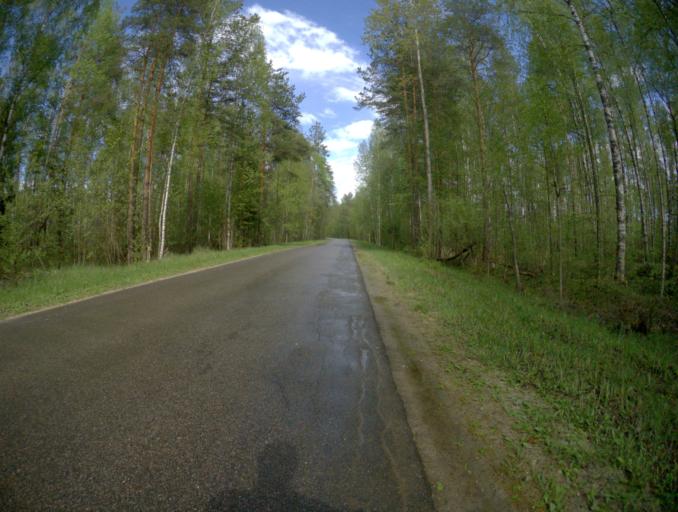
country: RU
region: Vladimir
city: Urshel'skiy
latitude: 55.5923
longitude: 40.2222
